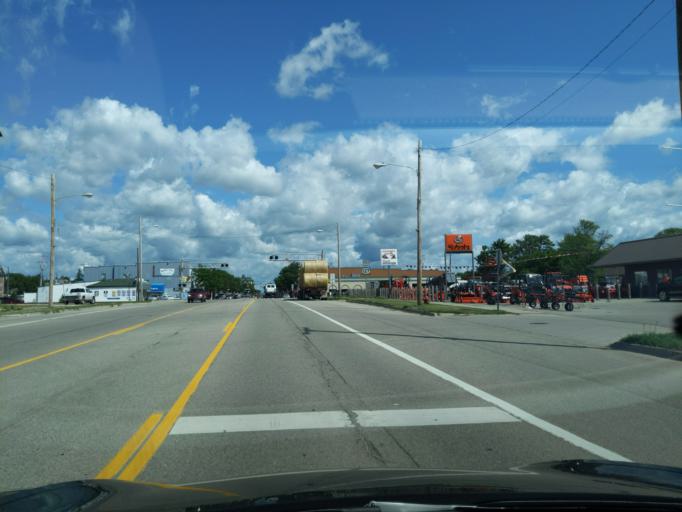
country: US
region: Michigan
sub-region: Clare County
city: Clare
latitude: 43.8168
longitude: -84.7683
